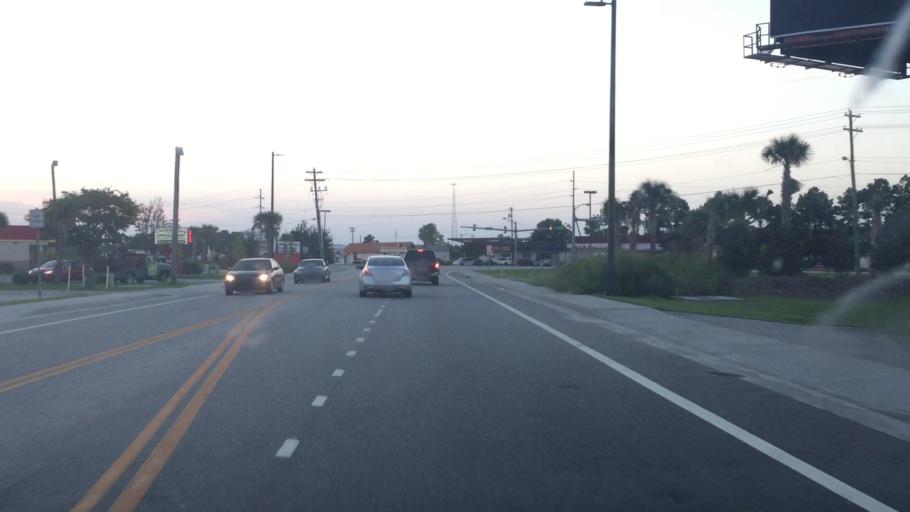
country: US
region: South Carolina
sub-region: Horry County
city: Myrtle Beach
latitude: 33.6979
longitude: -78.8990
